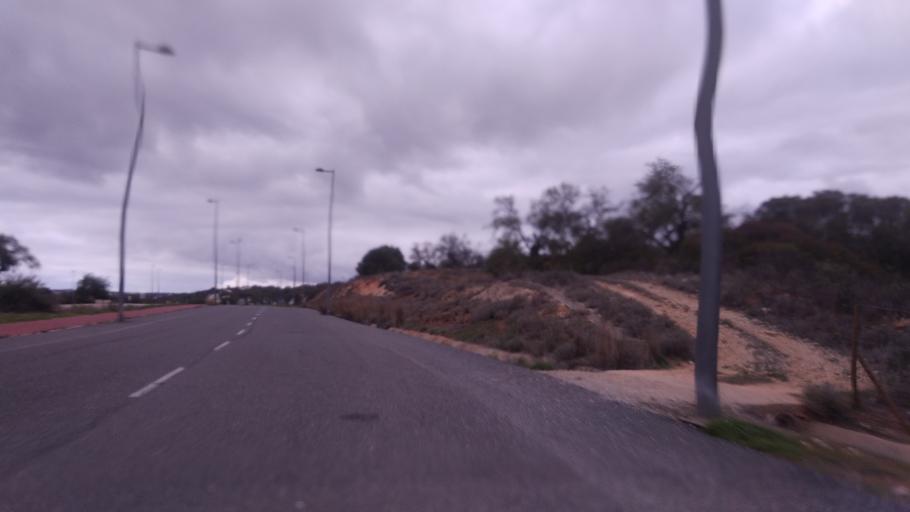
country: PT
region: Faro
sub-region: Faro
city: Santa Barbara de Nexe
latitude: 37.0909
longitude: -7.9756
